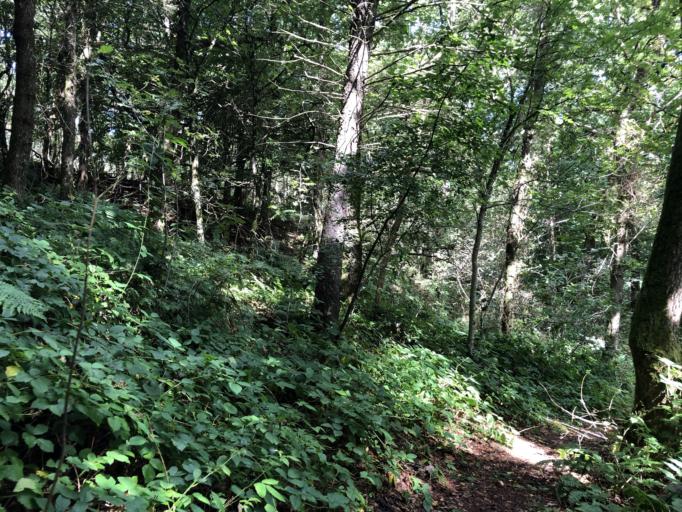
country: DK
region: Central Jutland
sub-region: Holstebro Kommune
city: Ulfborg
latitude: 56.3837
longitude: 8.3619
